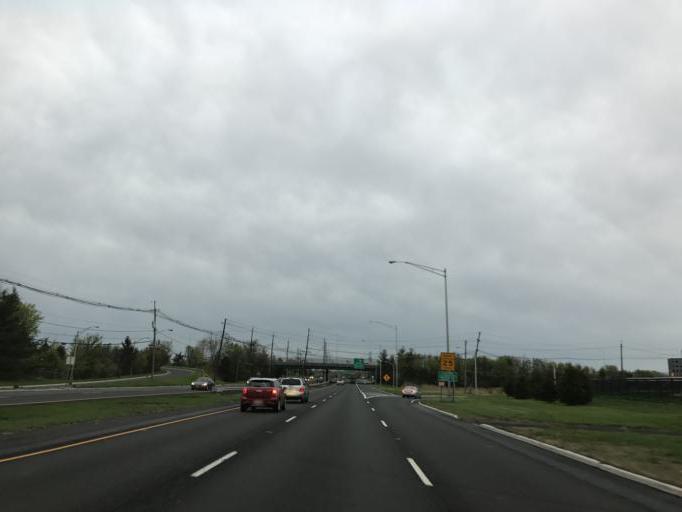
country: US
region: New Jersey
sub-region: Somerset County
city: Green Knoll
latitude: 40.5910
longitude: -74.6232
